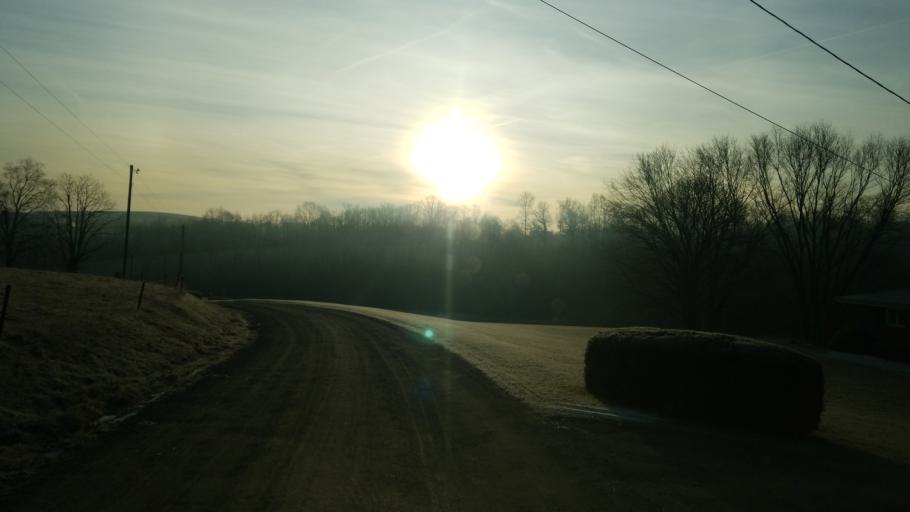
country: US
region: Pennsylvania
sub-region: Indiana County
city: Chevy Chase Heights
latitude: 40.8402
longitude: -79.1537
